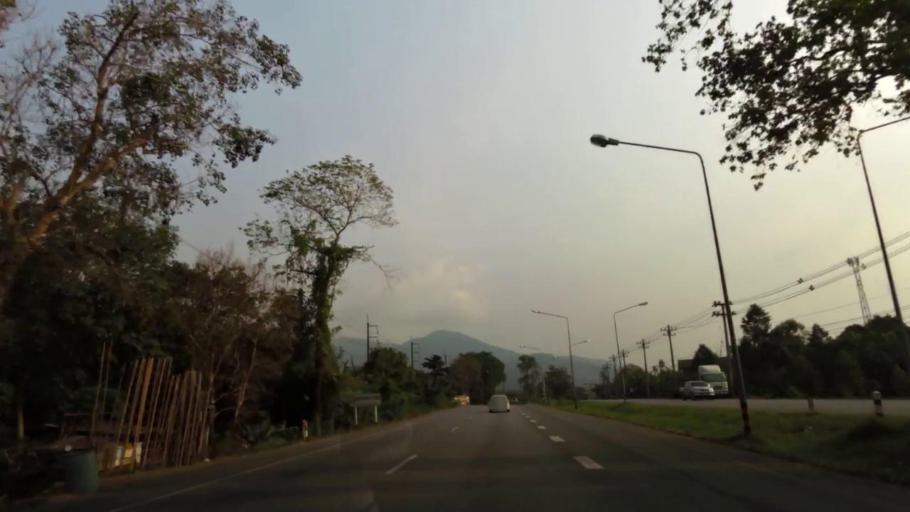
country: TH
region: Chanthaburi
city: Chanthaburi
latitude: 12.5846
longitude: 102.1572
